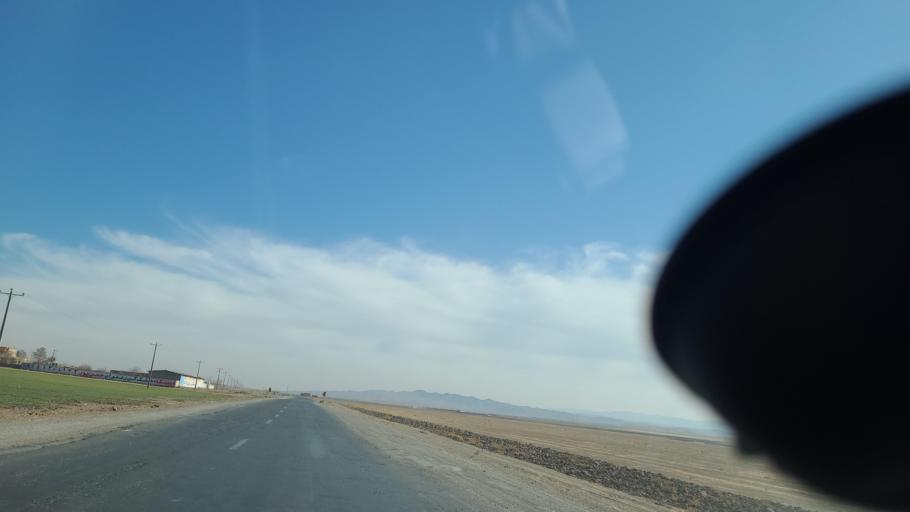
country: IR
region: Razavi Khorasan
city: Dowlatabad
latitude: 35.5998
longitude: 59.4680
